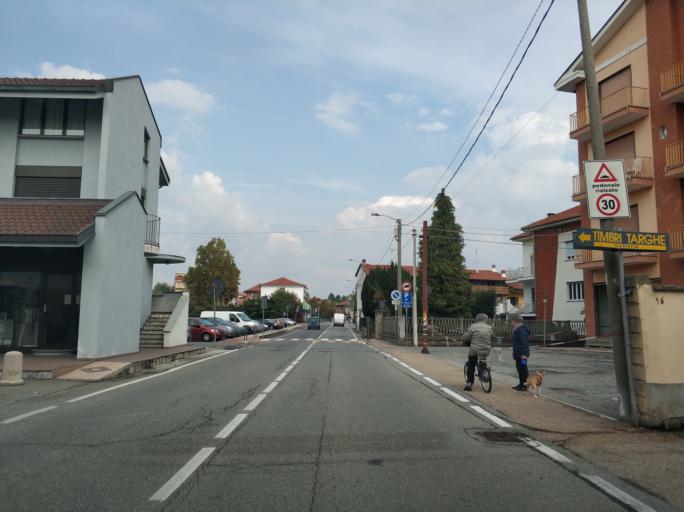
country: IT
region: Piedmont
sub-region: Provincia di Torino
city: San Carlo Canavese
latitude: 45.2385
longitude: 7.6044
